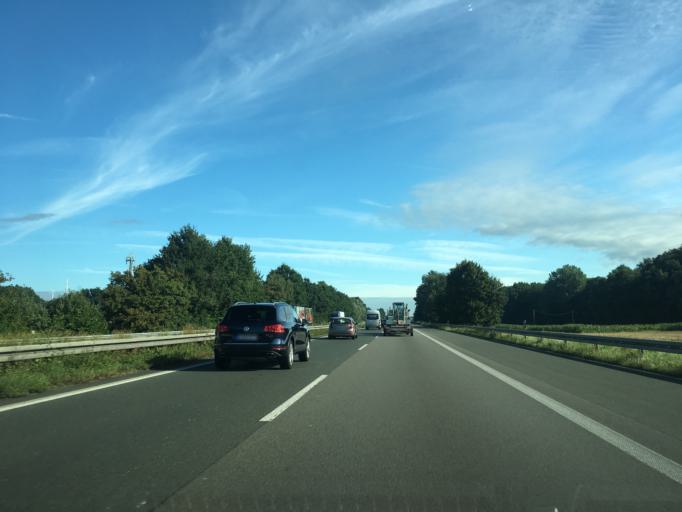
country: DE
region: North Rhine-Westphalia
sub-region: Regierungsbezirk Munster
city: Greven
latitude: 52.0369
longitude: 7.6056
